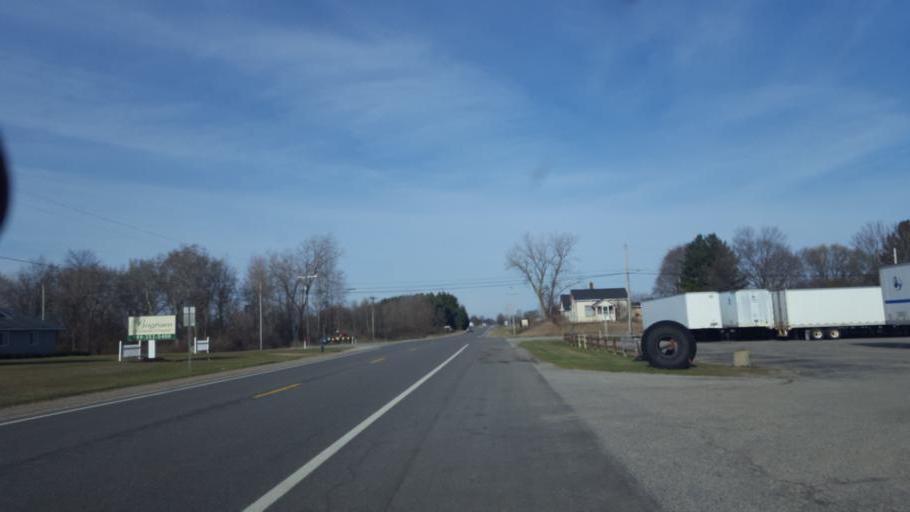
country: US
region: Michigan
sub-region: Montcalm County
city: Lakeview
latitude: 43.4315
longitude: -85.2822
